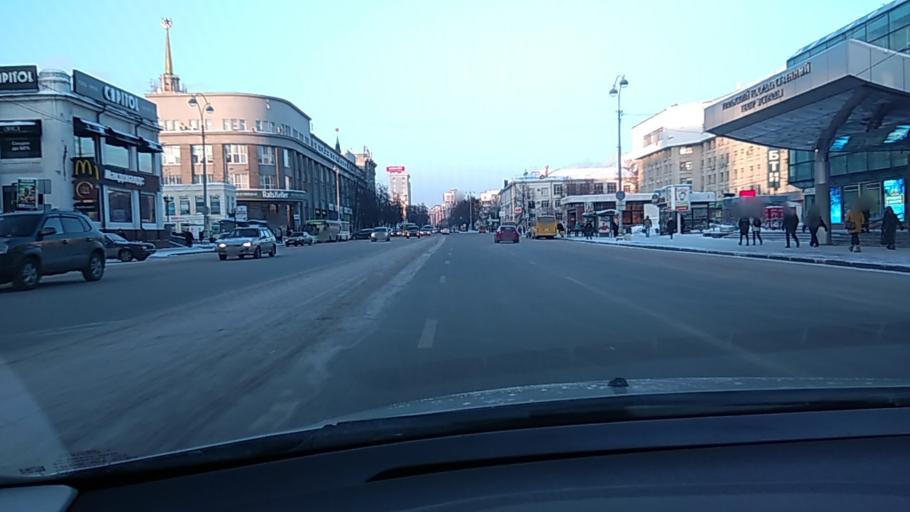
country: RU
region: Sverdlovsk
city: Yekaterinburg
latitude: 56.8353
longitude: 60.5997
